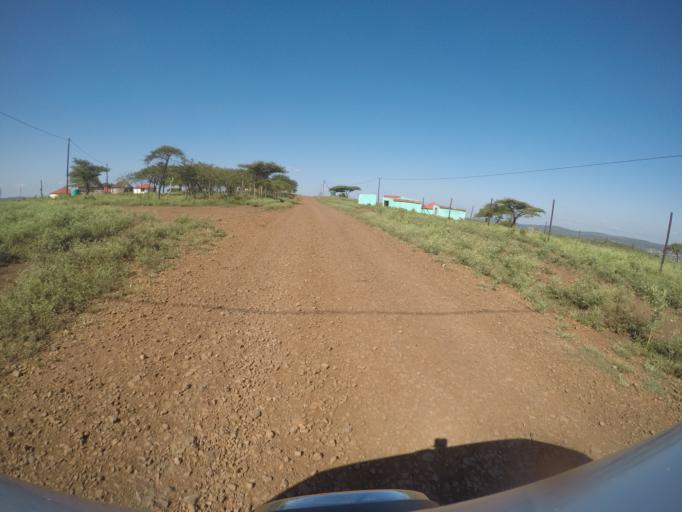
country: ZA
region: KwaZulu-Natal
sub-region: uThungulu District Municipality
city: Empangeni
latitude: -28.5716
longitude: 31.7313
